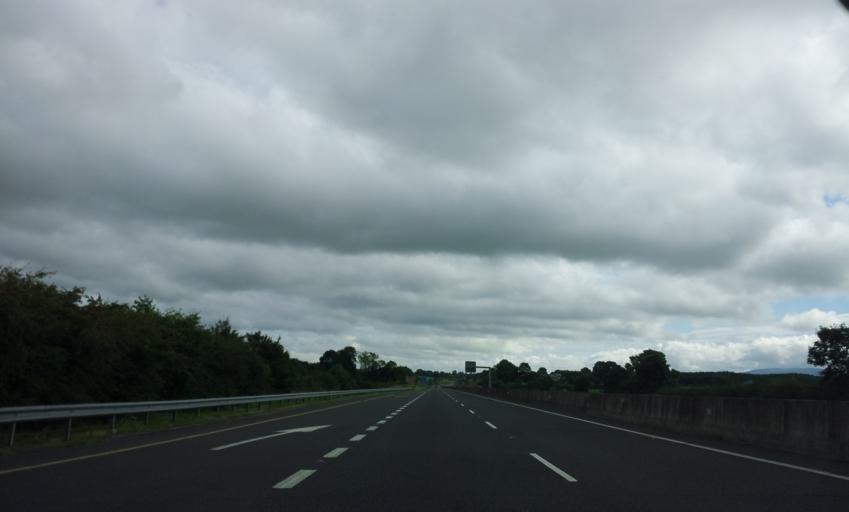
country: IE
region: Munster
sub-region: North Tipperary
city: Nenagh
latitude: 52.8517
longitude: -8.1501
